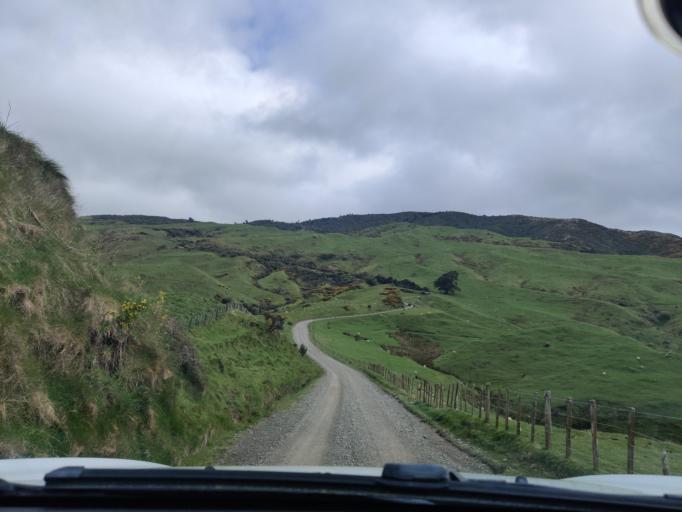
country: NZ
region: Manawatu-Wanganui
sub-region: Palmerston North City
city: Palmerston North
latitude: -40.2826
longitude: 175.8572
